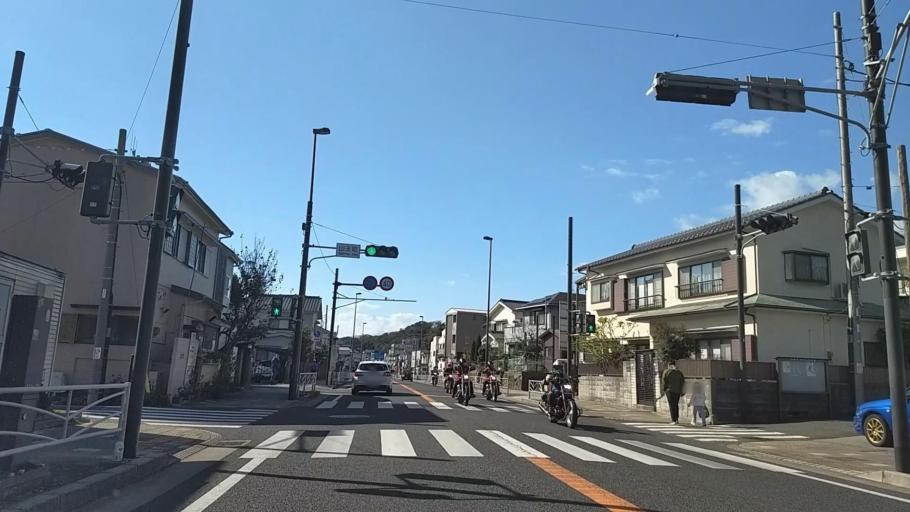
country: JP
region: Kanagawa
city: Oiso
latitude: 35.3133
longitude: 139.3193
